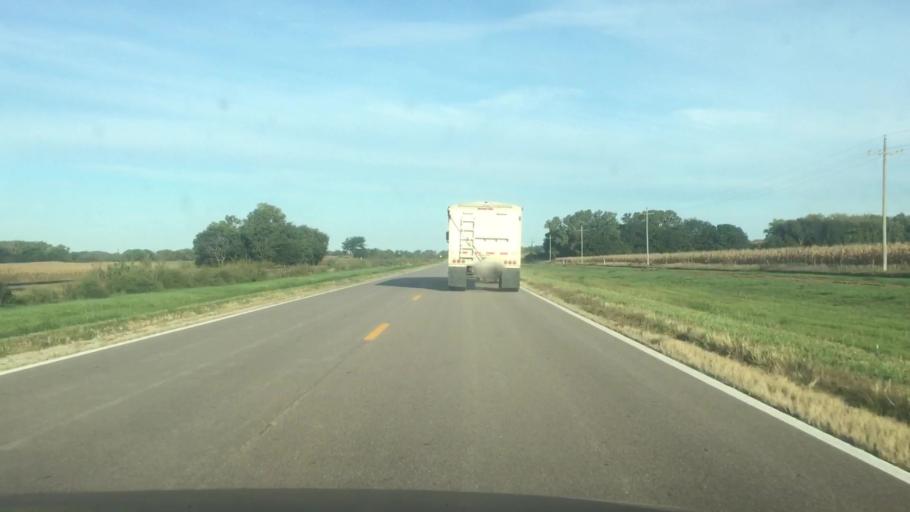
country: US
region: Nebraska
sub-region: Jefferson County
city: Fairbury
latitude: 40.0537
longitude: -97.0356
